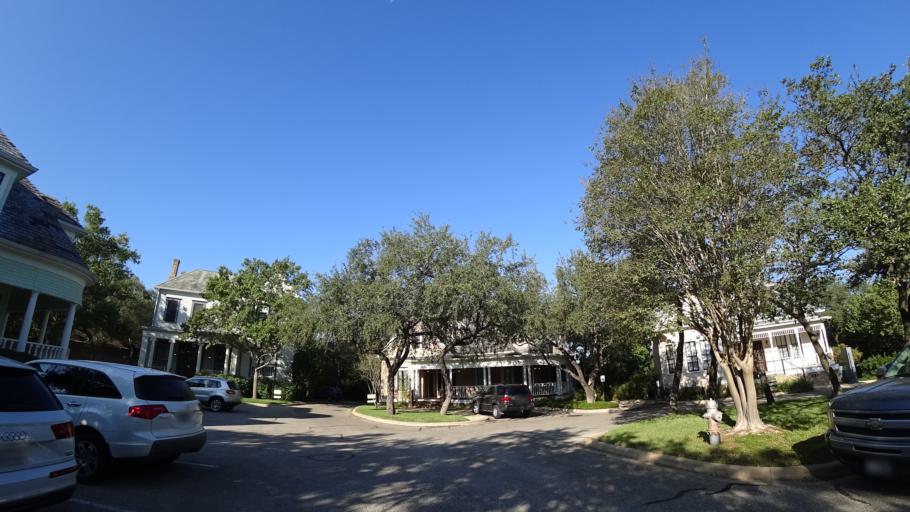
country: US
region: Texas
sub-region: Travis County
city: Rollingwood
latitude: 30.2698
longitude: -97.7919
